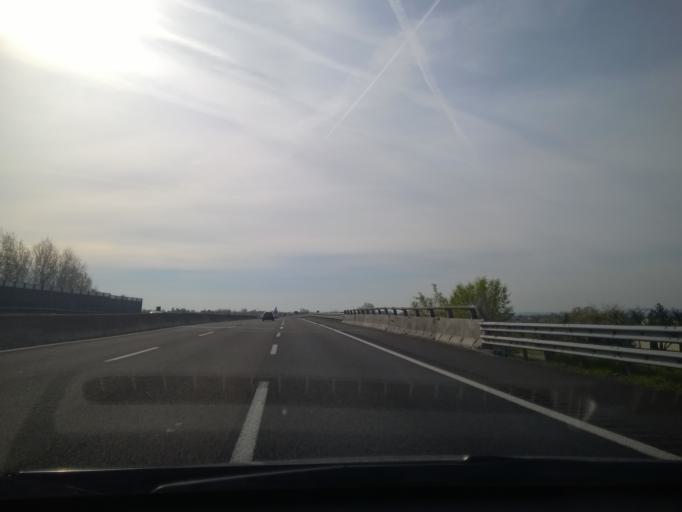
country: IT
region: Emilia-Romagna
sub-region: Provincia di Ravenna
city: Granarolo
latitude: 44.3135
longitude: 11.9272
